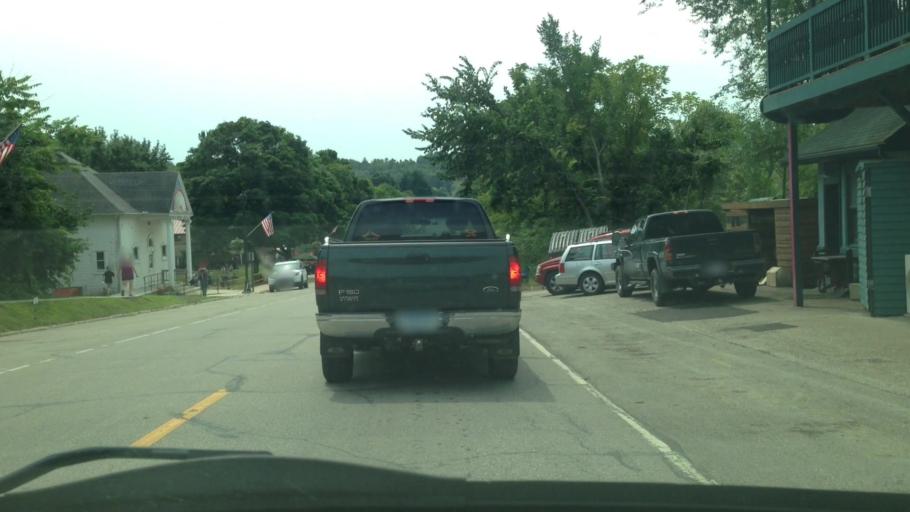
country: US
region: Minnesota
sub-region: Fillmore County
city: Preston
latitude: 43.7203
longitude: -91.9770
